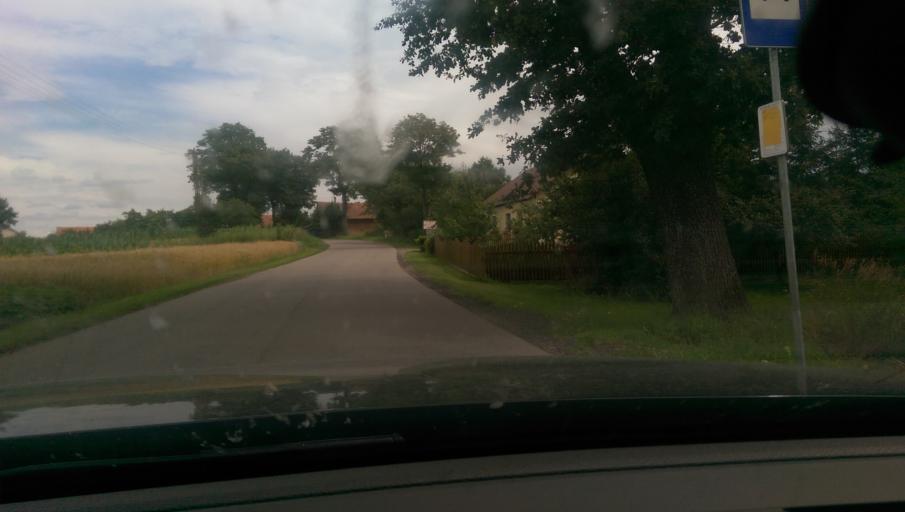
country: PL
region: Podlasie
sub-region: Powiat suwalski
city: Raczki
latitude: 53.9381
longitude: 22.6922
